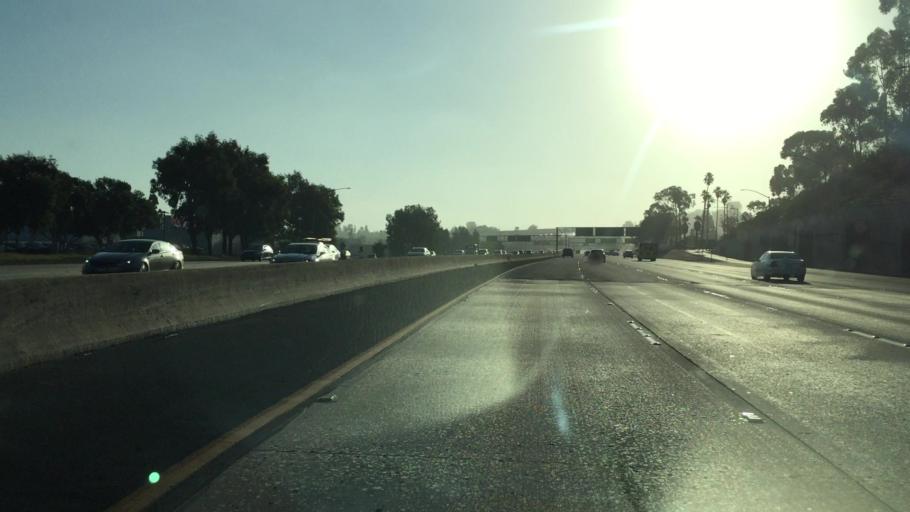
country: US
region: California
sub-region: San Diego County
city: La Mesa
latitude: 32.7734
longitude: -117.0153
